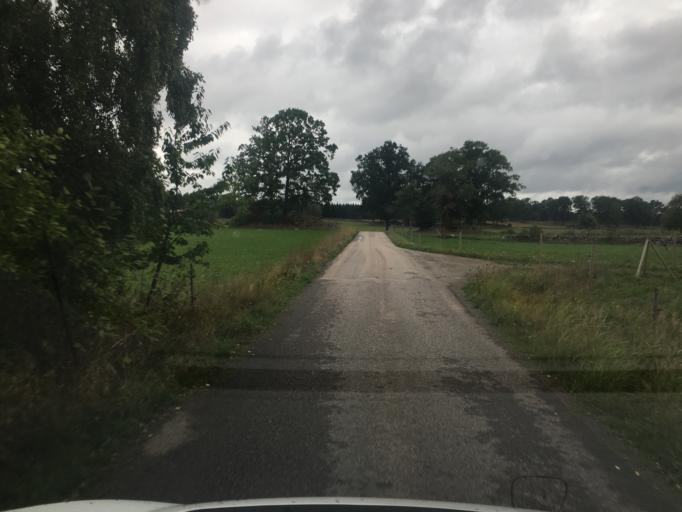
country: SE
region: Kronoberg
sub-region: Ljungby Kommun
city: Lagan
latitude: 56.9769
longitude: 14.0375
